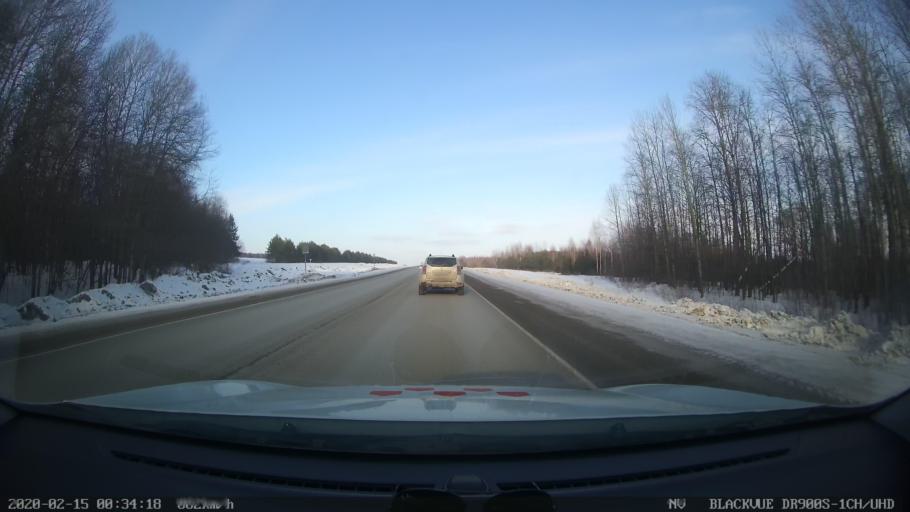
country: RU
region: Tatarstan
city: Verkhniy Uslon
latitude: 55.6973
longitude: 48.8832
